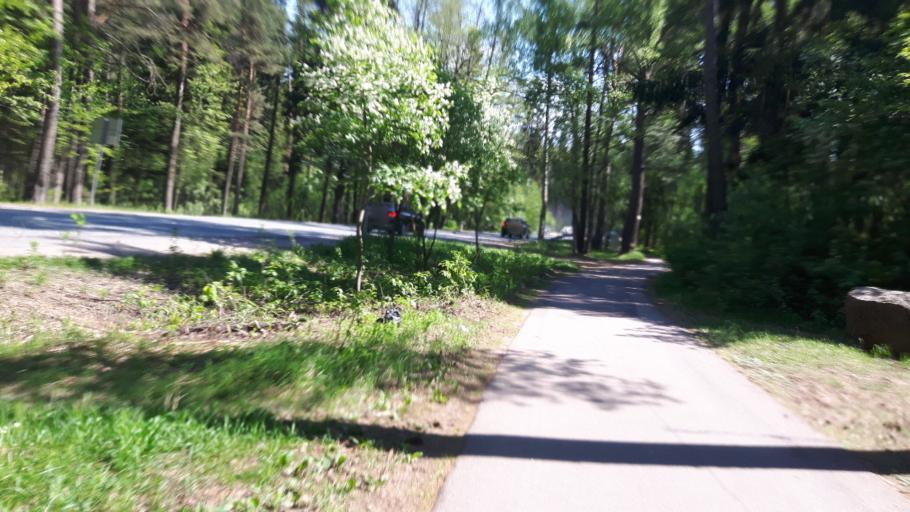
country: RU
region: St.-Petersburg
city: Komarovo
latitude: 60.1717
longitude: 29.8110
